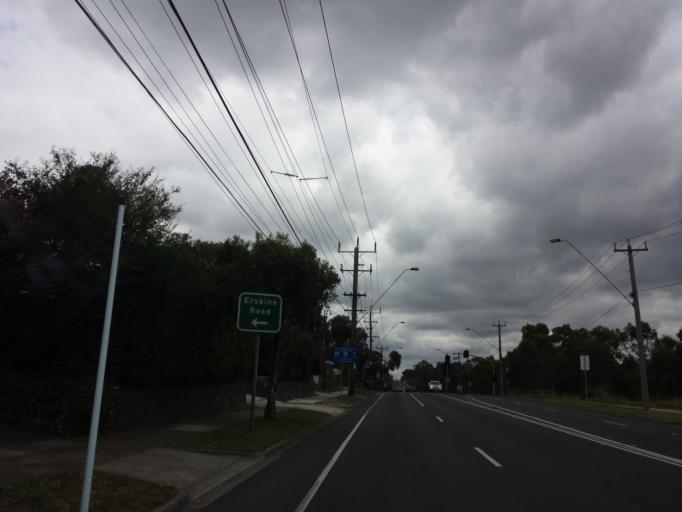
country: AU
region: Victoria
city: Macleod
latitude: -37.7307
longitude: 145.0792
